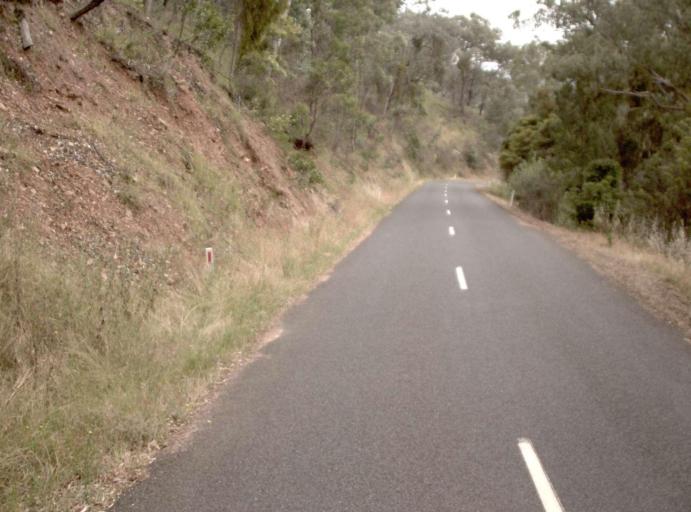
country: AU
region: Victoria
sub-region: Wellington
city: Heyfield
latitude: -37.8066
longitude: 146.6714
